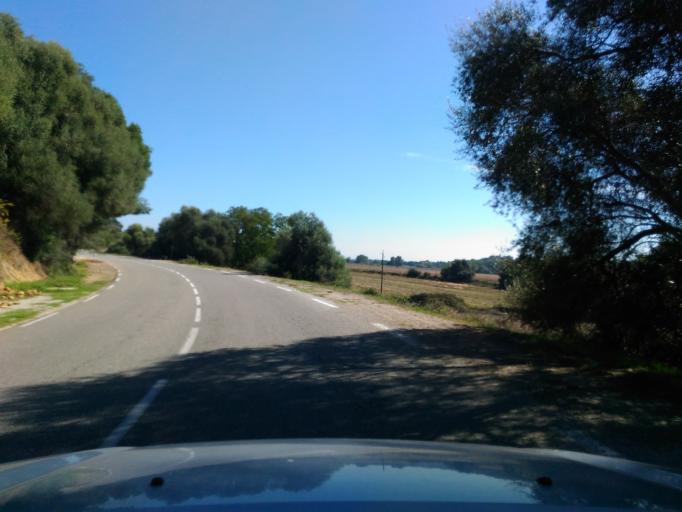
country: FR
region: Corsica
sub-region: Departement de la Haute-Corse
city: Aleria
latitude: 42.1140
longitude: 9.4941
